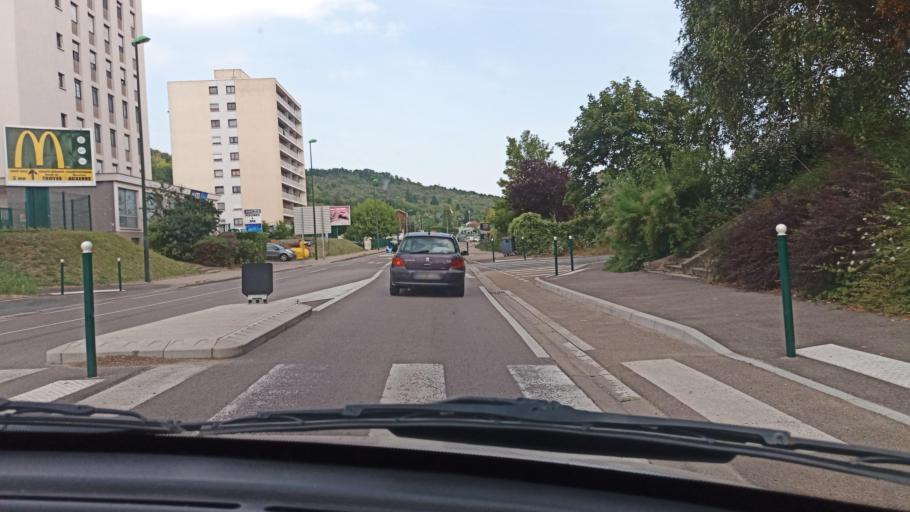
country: FR
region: Bourgogne
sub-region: Departement de l'Yonne
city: Sens
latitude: 48.1964
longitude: 3.2658
